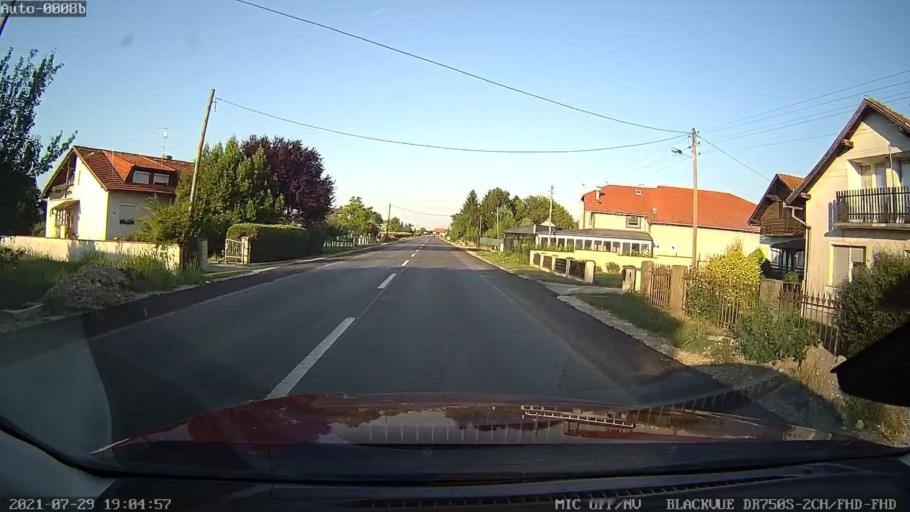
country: HR
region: Medimurska
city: Kursanec
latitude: 46.2979
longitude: 16.4405
